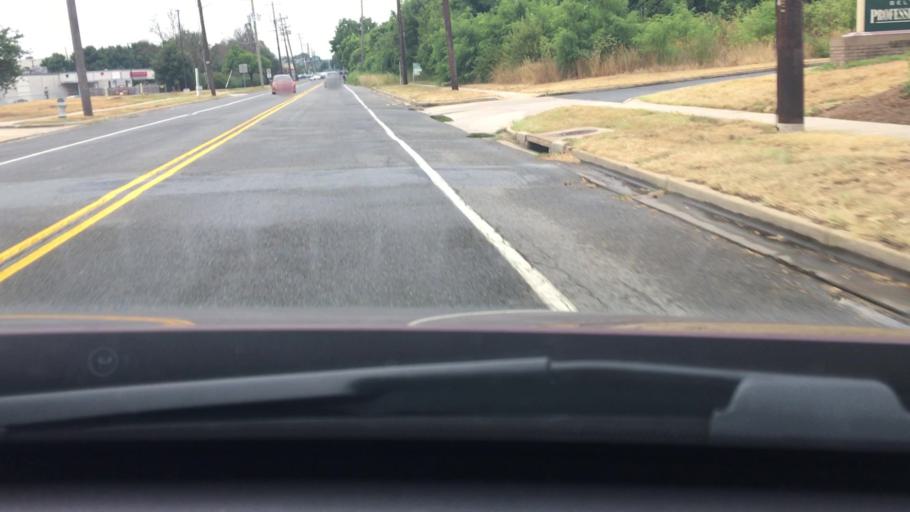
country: US
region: Maryland
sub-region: Prince George's County
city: Beltsville
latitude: 39.0321
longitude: -76.9142
